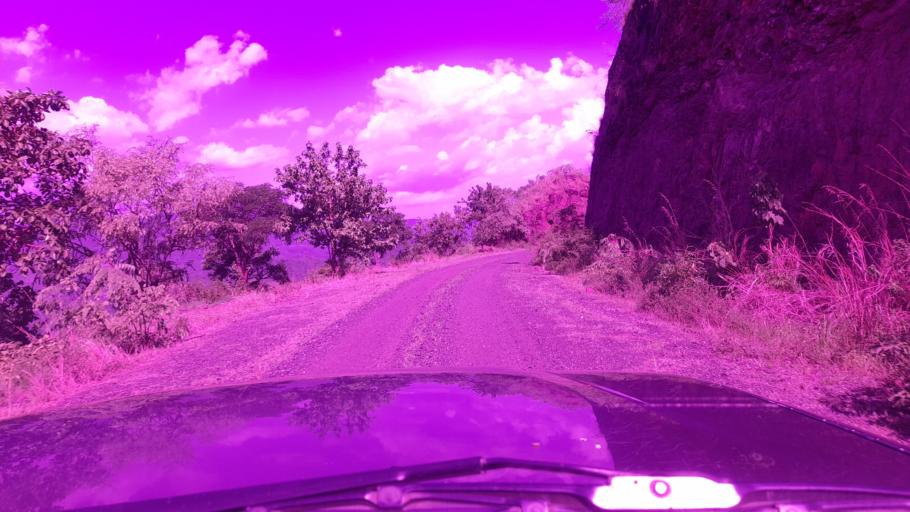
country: ET
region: Southern Nations, Nationalities, and People's Region
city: K'olito
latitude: 7.7799
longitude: 37.5590
